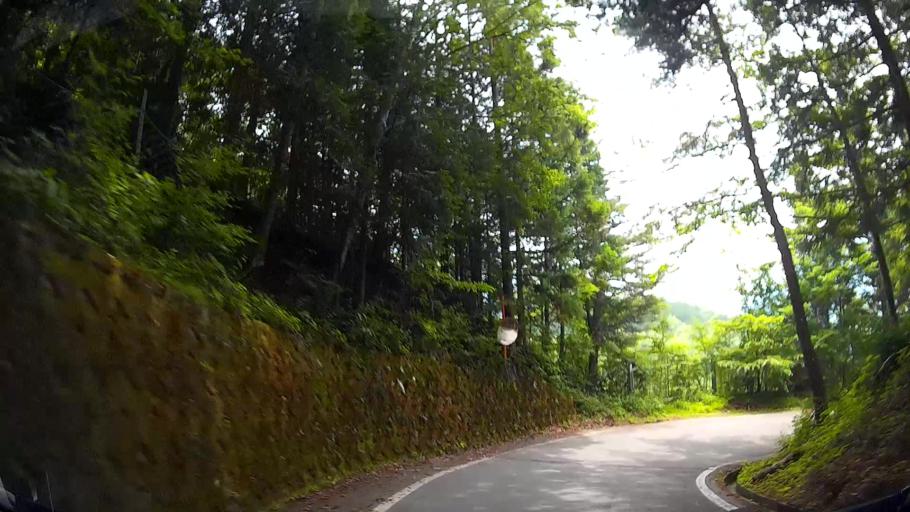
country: JP
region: Nagano
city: Iida
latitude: 35.2668
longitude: 137.9217
